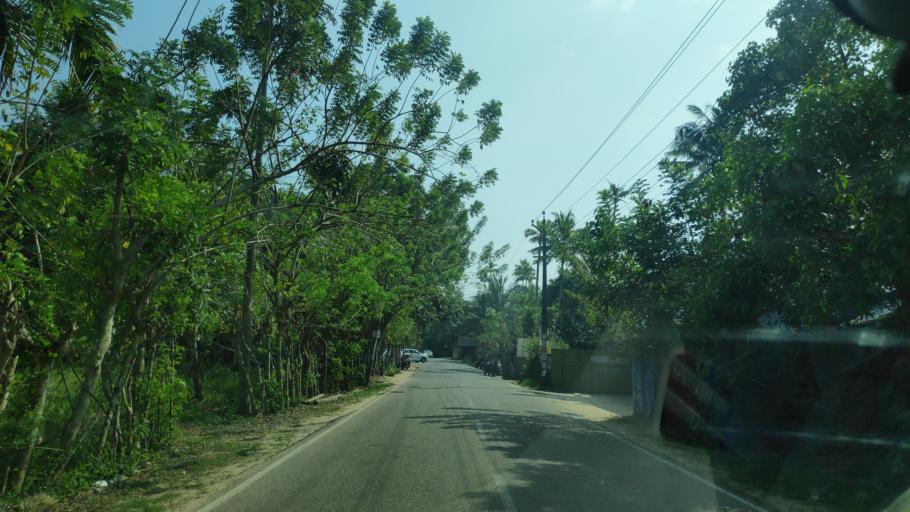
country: IN
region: Kerala
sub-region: Alappuzha
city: Shertallai
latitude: 9.6283
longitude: 76.2996
